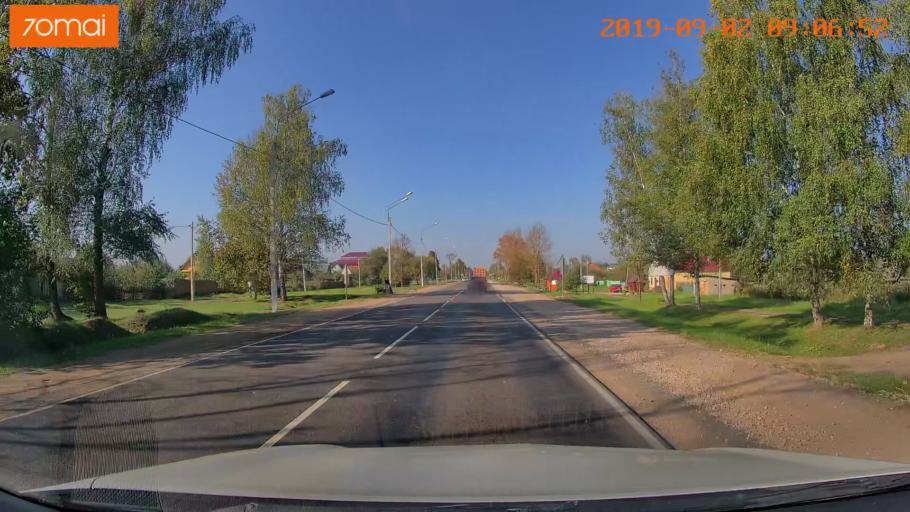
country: RU
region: Kaluga
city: Myatlevo
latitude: 54.8983
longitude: 35.6652
